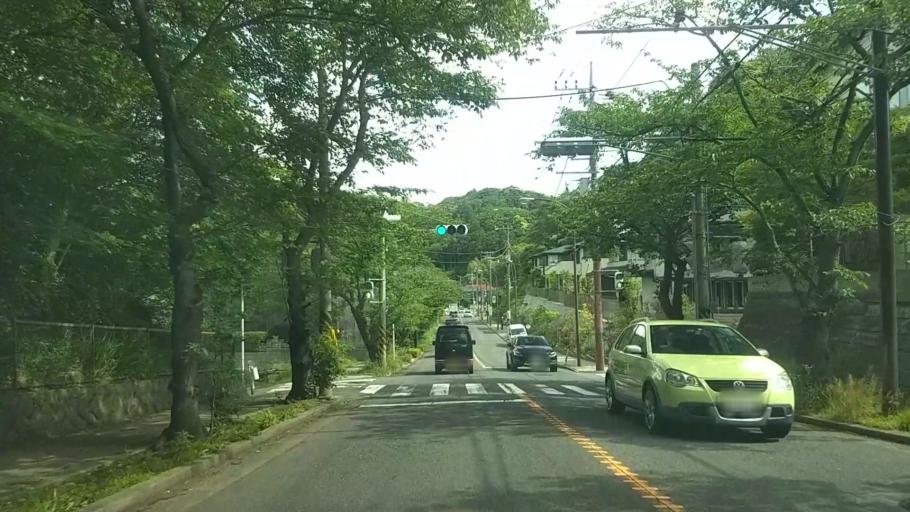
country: JP
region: Kanagawa
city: Zushi
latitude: 35.3173
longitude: 139.5767
